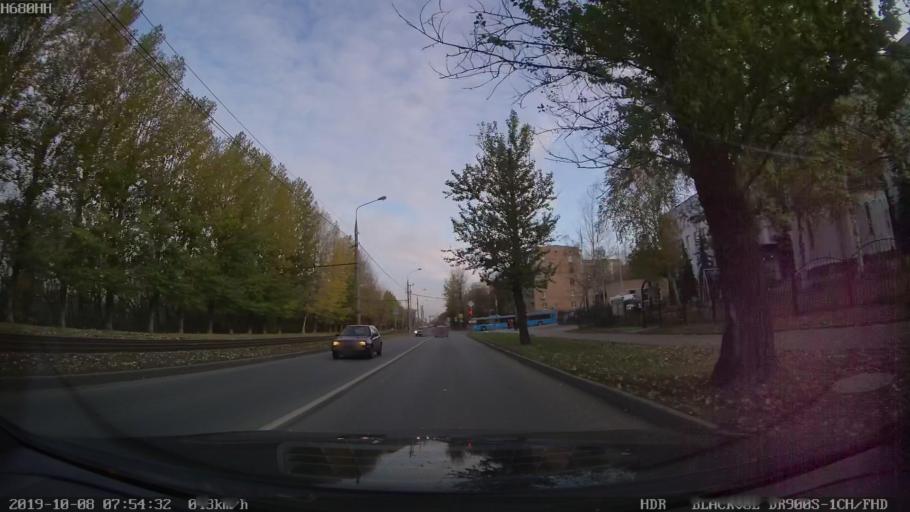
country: RU
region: Moscow
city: Shchukino
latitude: 55.7910
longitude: 37.4543
